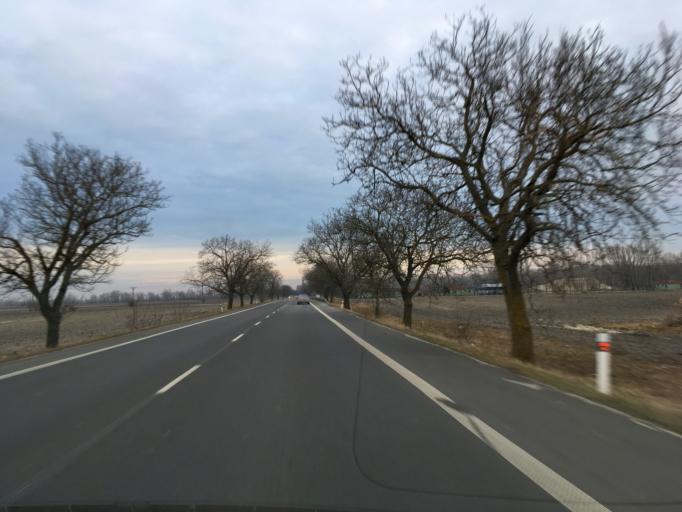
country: SK
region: Trnavsky
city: Dunajska Streda
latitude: 47.9553
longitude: 17.7020
